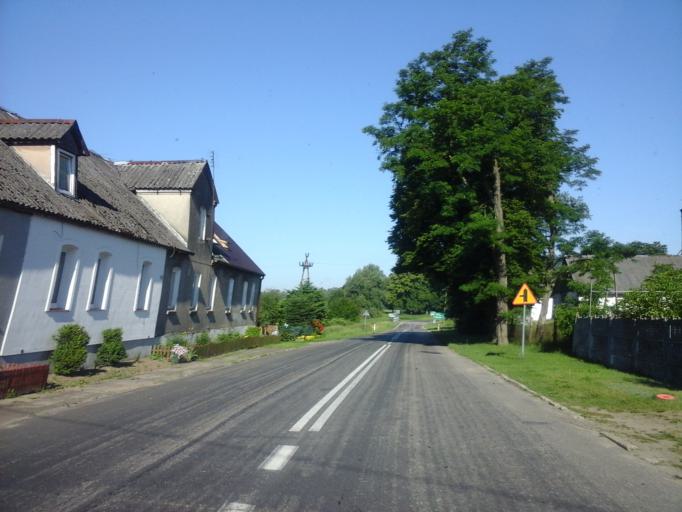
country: PL
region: West Pomeranian Voivodeship
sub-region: Powiat stargardzki
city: Insko
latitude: 53.3985
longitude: 15.5711
